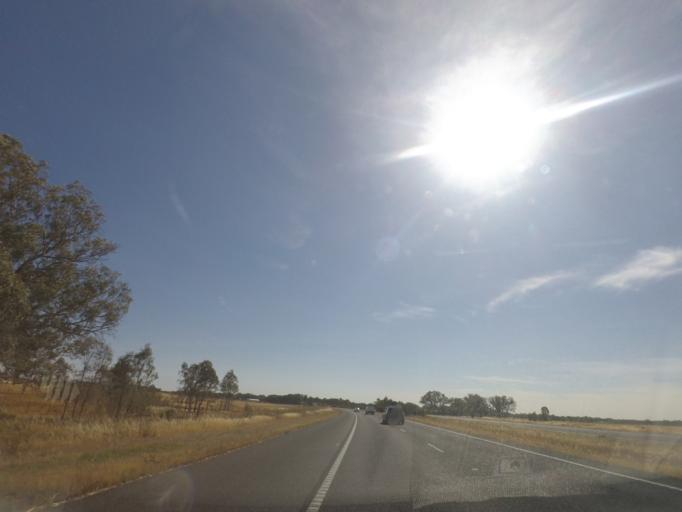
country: AU
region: Victoria
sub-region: Greater Shepparton
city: Shepparton
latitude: -36.6753
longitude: 145.2494
